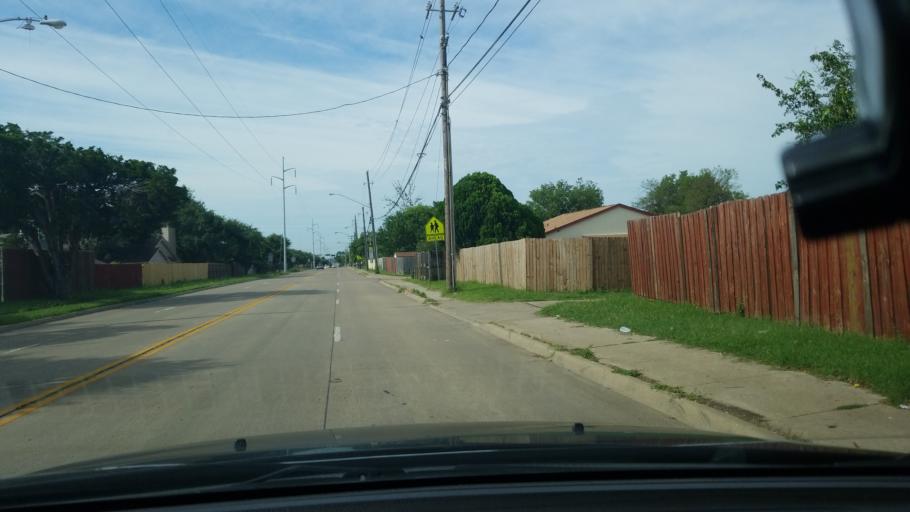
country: US
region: Texas
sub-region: Dallas County
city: Balch Springs
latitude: 32.7659
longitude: -96.6569
